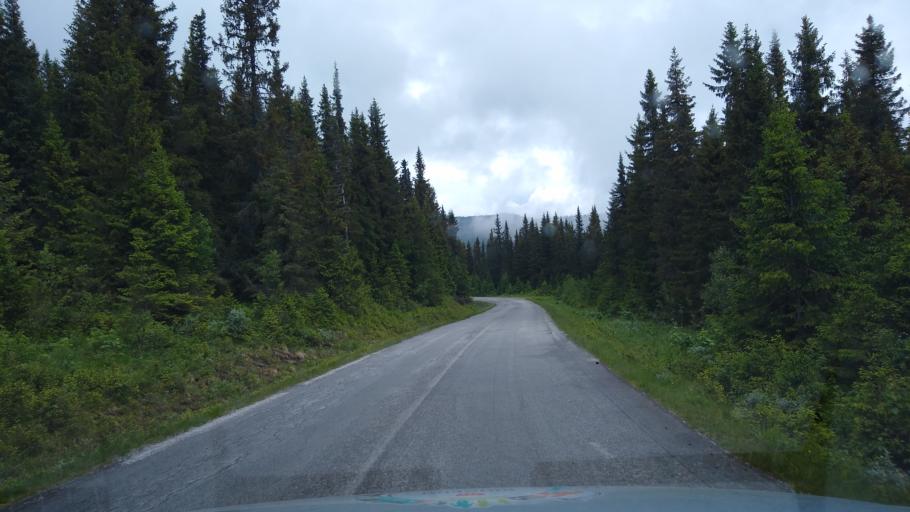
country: NO
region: Oppland
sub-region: Ringebu
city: Ringebu
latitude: 61.4851
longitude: 10.1162
